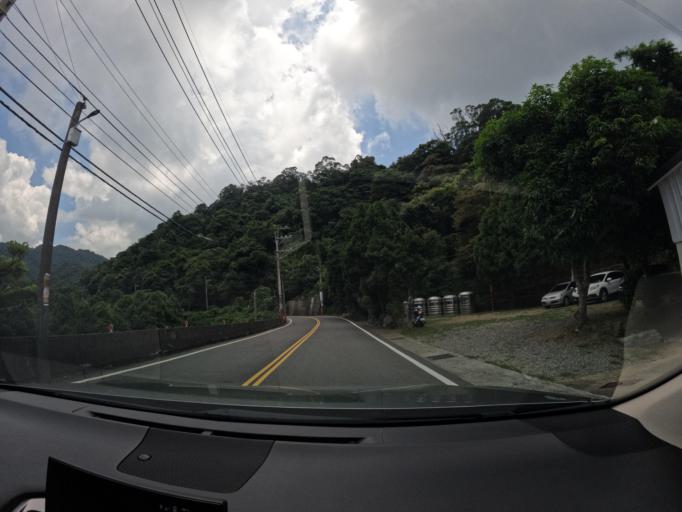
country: TW
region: Taiwan
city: Fengyuan
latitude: 24.3836
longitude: 120.8059
